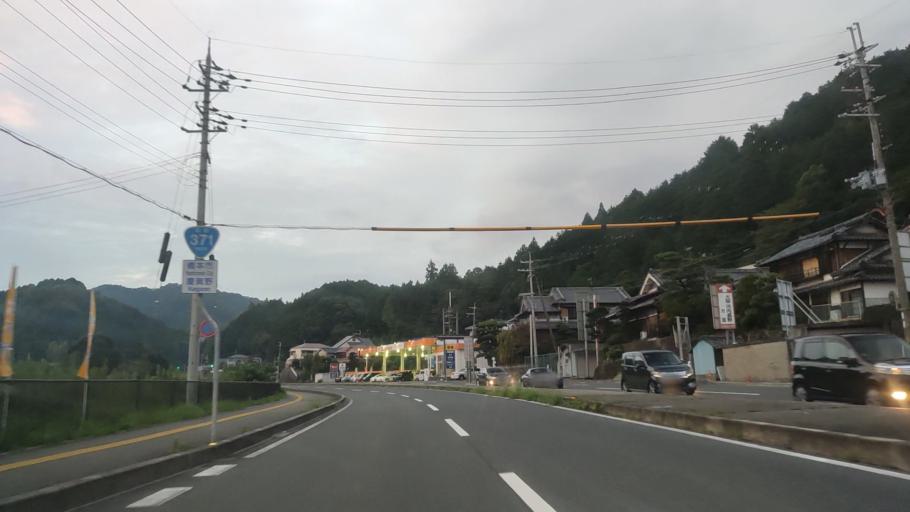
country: JP
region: Wakayama
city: Hashimoto
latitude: 34.3588
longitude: 135.6069
